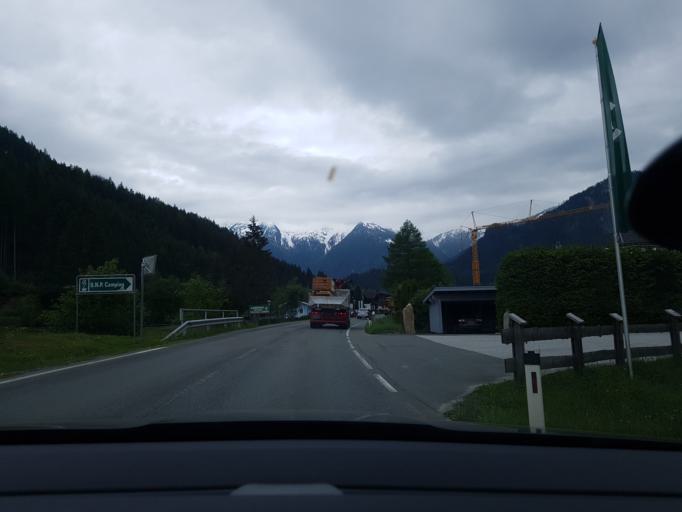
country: AT
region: Salzburg
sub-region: Politischer Bezirk Zell am See
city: Wald im Pinzgau
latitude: 47.2430
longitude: 12.2121
